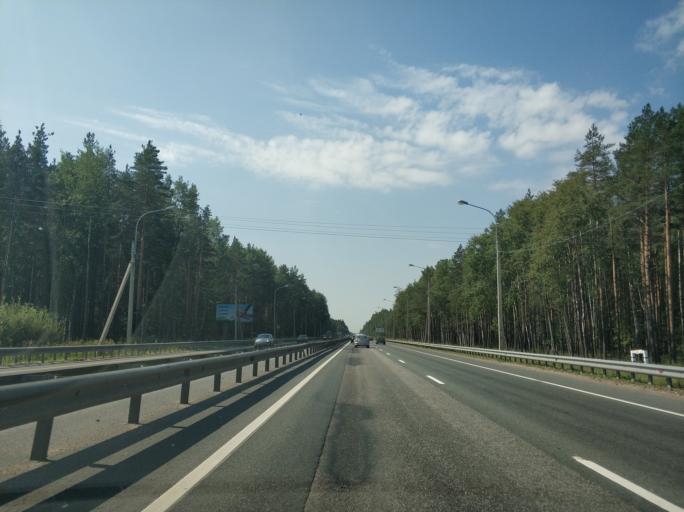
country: RU
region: Leningrad
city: Yanino Vtoroye
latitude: 60.0046
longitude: 30.5635
